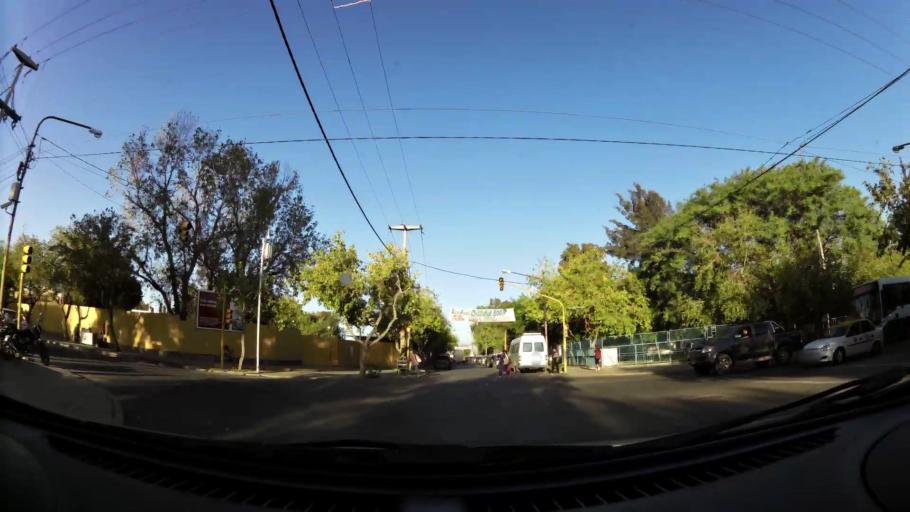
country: AR
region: San Juan
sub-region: Departamento de Santa Lucia
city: Santa Lucia
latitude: -31.5404
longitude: -68.5117
